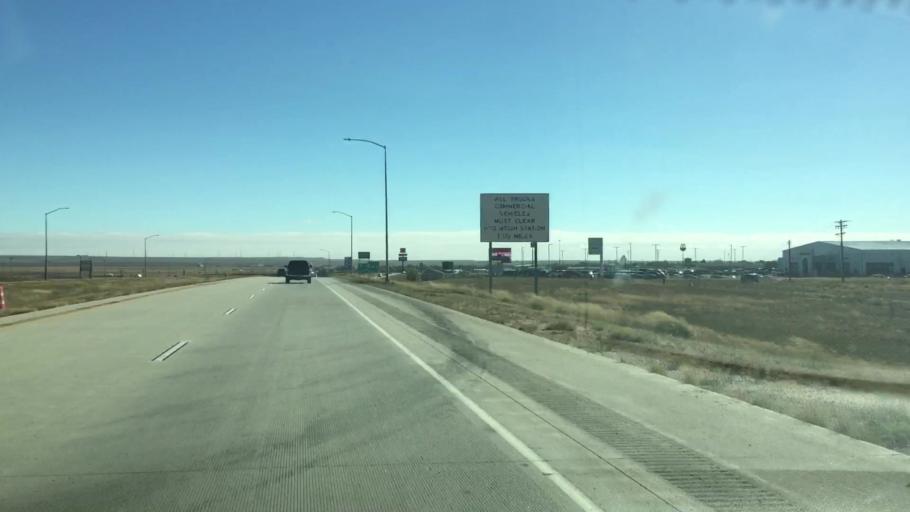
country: US
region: Colorado
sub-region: Lincoln County
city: Limon
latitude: 39.2732
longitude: -103.7163
